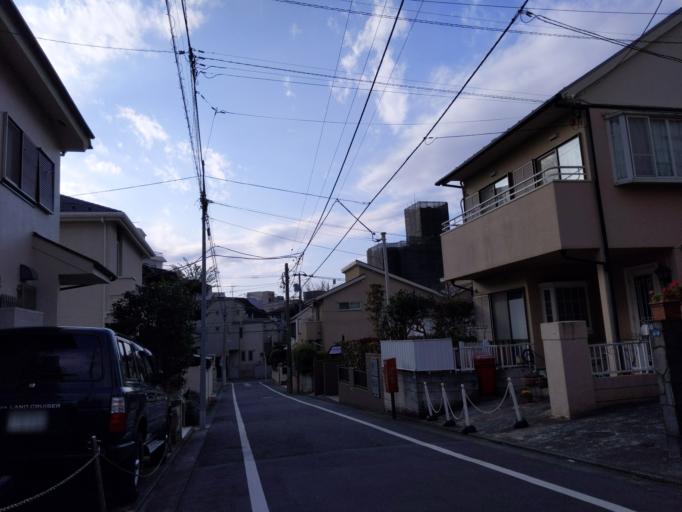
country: JP
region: Tokyo
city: Tokyo
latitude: 35.6102
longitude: 139.6967
